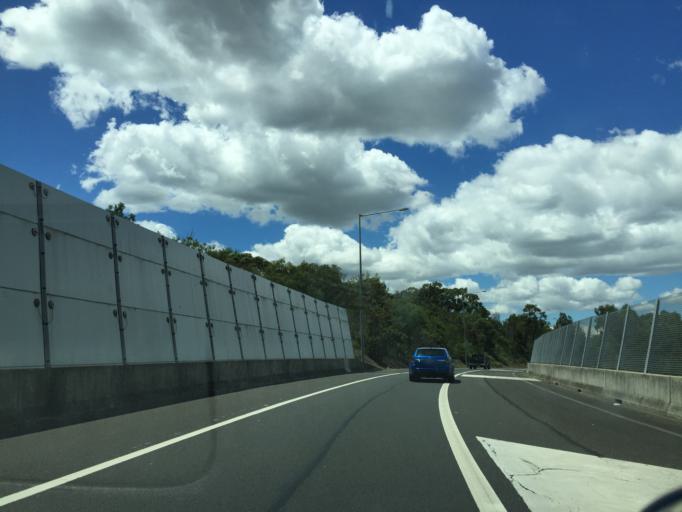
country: AU
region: New South Wales
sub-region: Parramatta
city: Northmead
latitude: -33.7655
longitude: 150.9633
